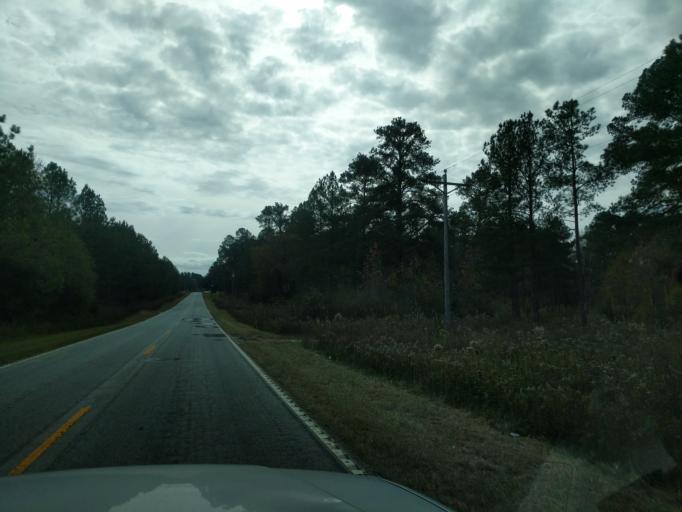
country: US
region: South Carolina
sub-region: Laurens County
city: Joanna
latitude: 34.3309
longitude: -81.8517
